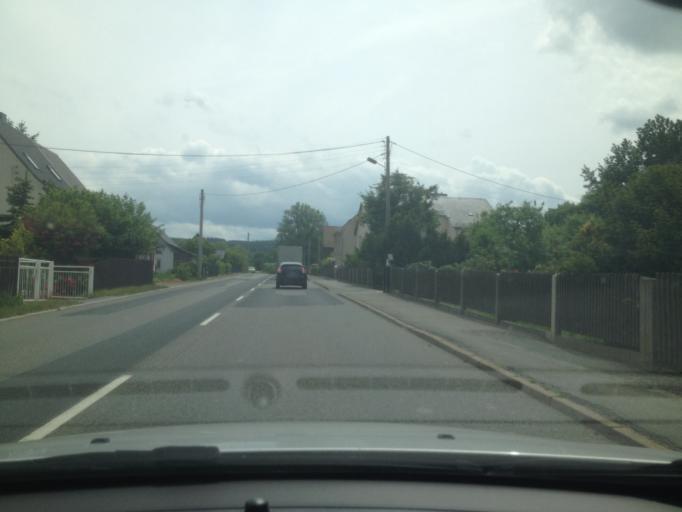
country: DE
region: Saxony
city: Stollberg
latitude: 50.6808
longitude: 12.7631
